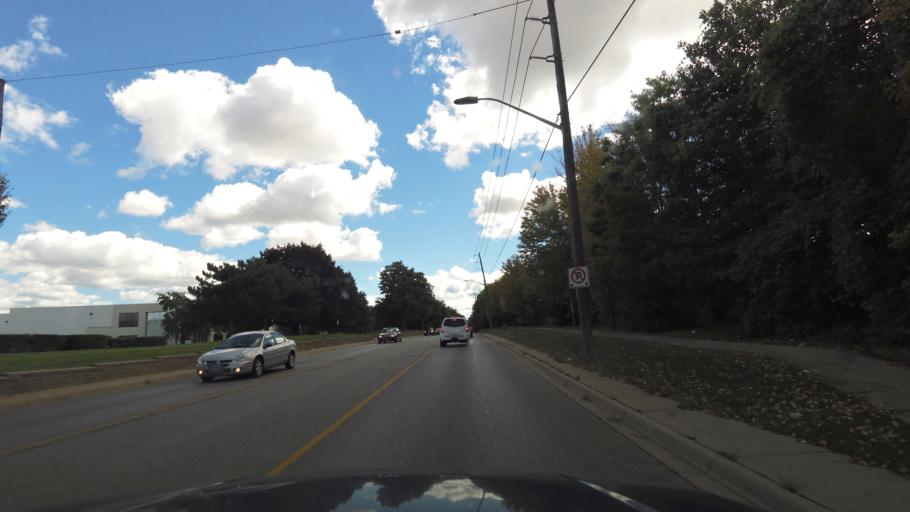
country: CA
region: Ontario
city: Mississauga
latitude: 43.6121
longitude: -79.6838
